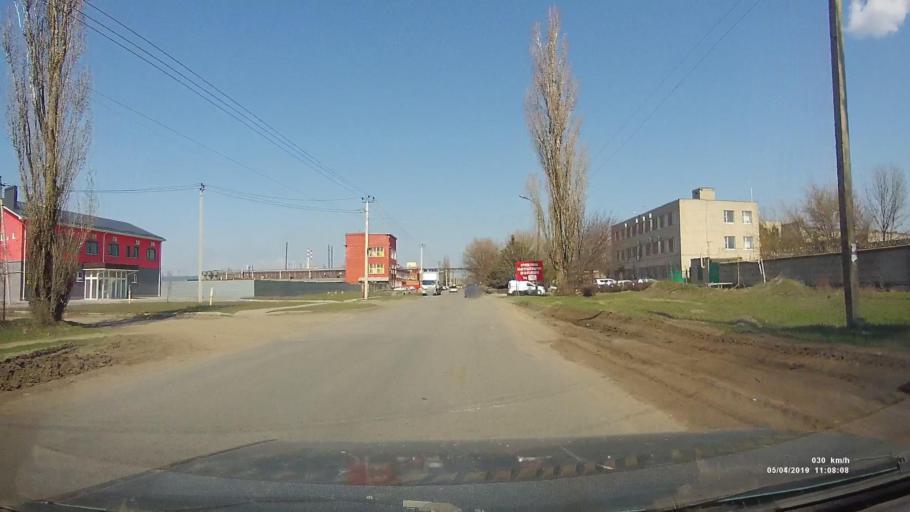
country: RU
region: Rostov
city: Azov
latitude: 47.0844
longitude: 39.4363
